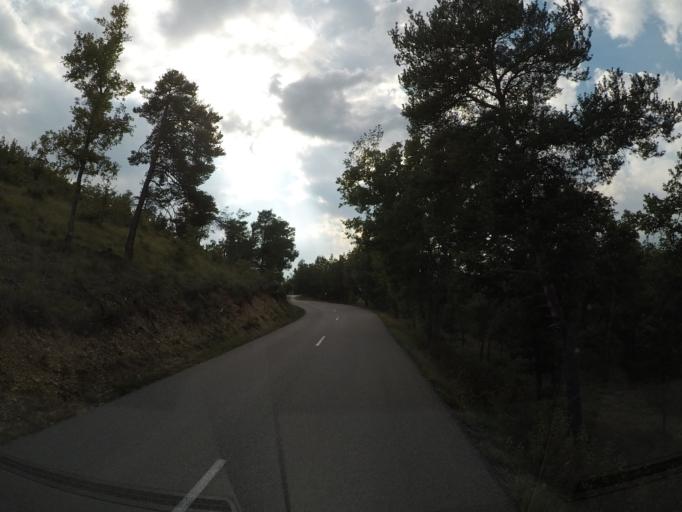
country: FR
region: Provence-Alpes-Cote d'Azur
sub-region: Departement des Alpes-de-Haute-Provence
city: Riez
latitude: 43.8289
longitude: 6.0438
